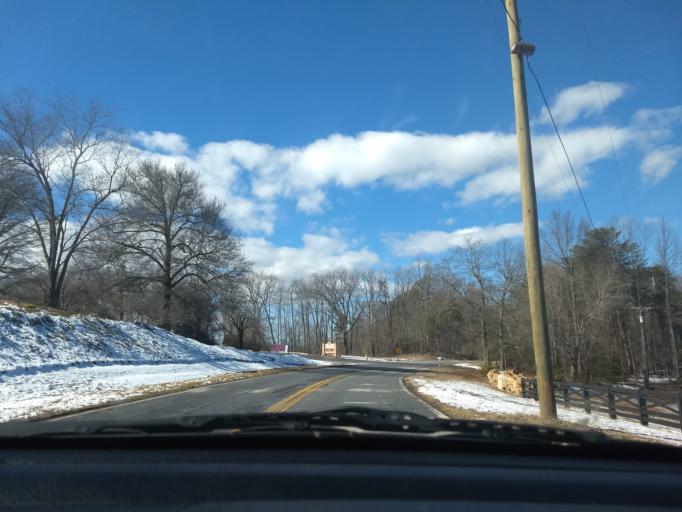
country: US
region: South Carolina
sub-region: Greenville County
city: Greenville
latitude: 34.8979
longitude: -82.3806
